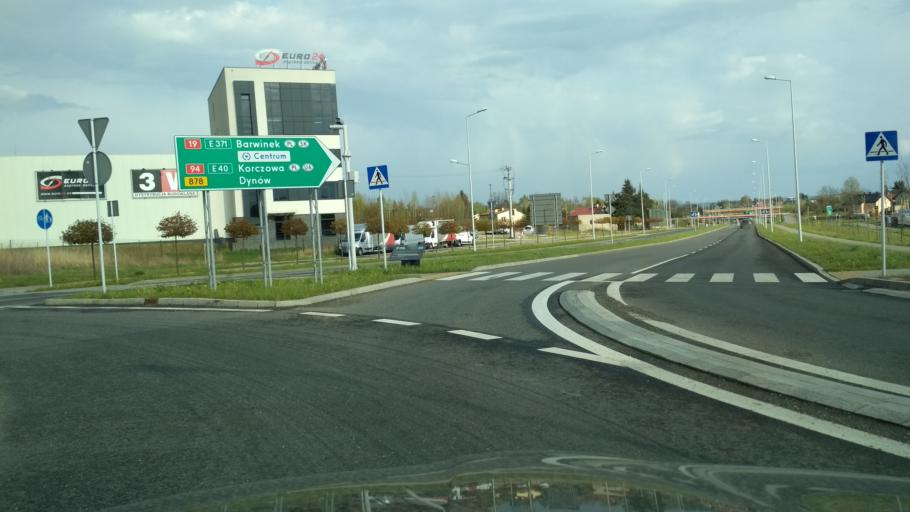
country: PL
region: Subcarpathian Voivodeship
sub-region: Powiat rzeszowski
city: Boguchwala
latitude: 50.0141
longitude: 21.9592
